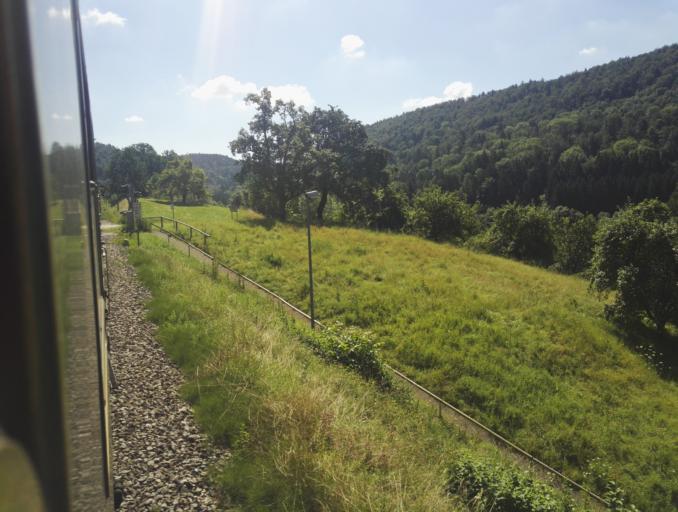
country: DE
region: Baden-Wuerttemberg
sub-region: Regierungsbezirk Stuttgart
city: Althutte
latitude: 48.8991
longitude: 9.5769
